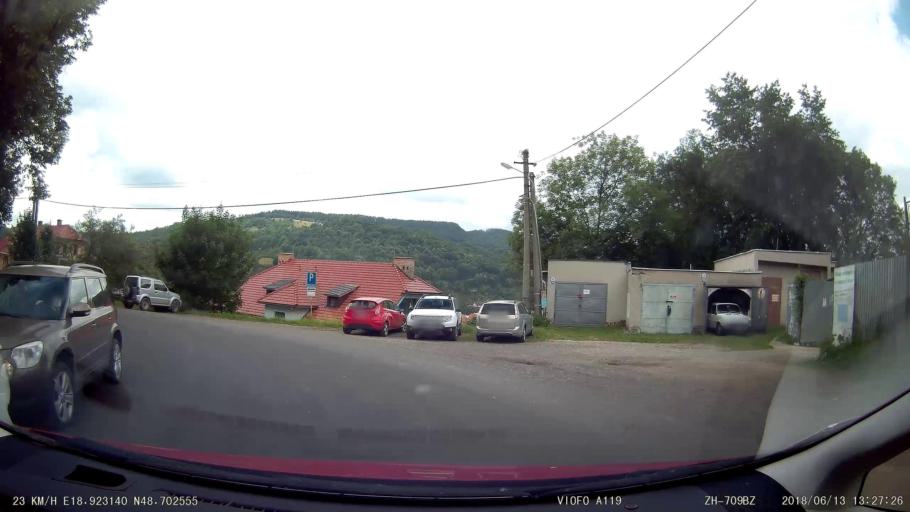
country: SK
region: Banskobystricky
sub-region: Okres Ziar nad Hronom
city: Kremnica
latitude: 48.7029
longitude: 18.9234
